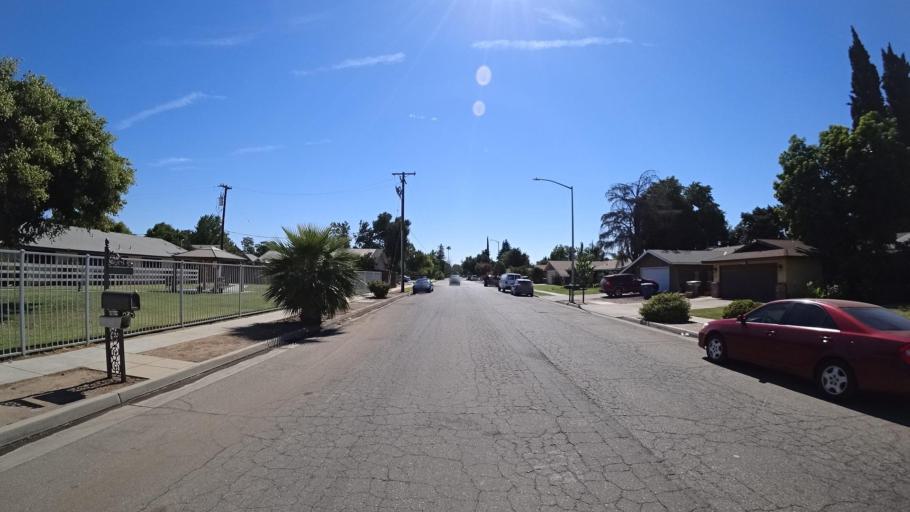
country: US
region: California
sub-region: Fresno County
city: Sunnyside
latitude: 36.7395
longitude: -119.7158
